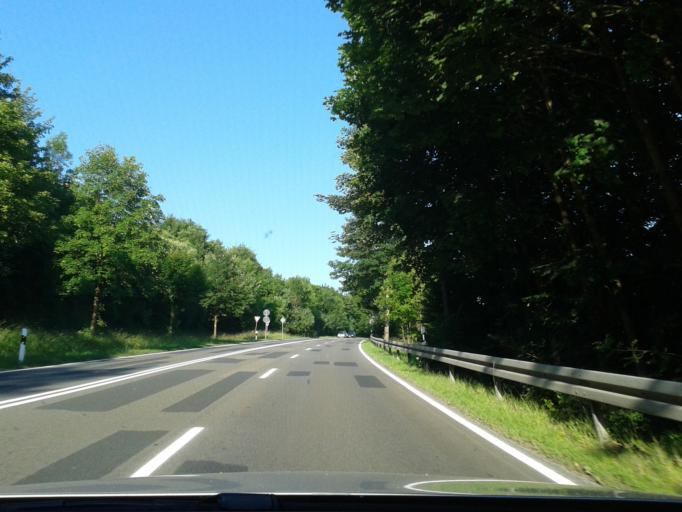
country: DE
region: North Rhine-Westphalia
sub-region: Regierungsbezirk Detmold
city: Lugde
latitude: 51.9772
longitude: 9.2047
